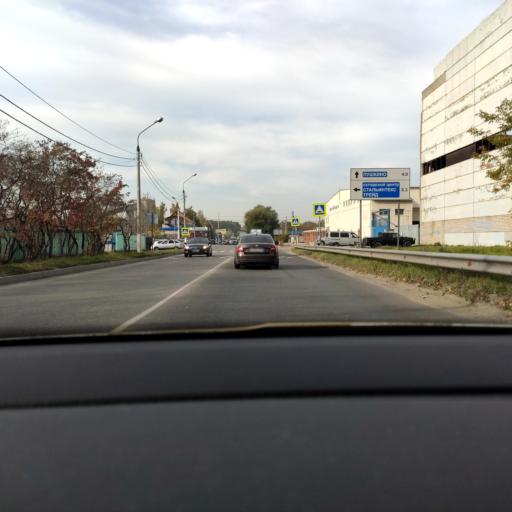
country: RU
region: Moskovskaya
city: Ivanteyevka
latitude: 55.9674
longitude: 37.8949
